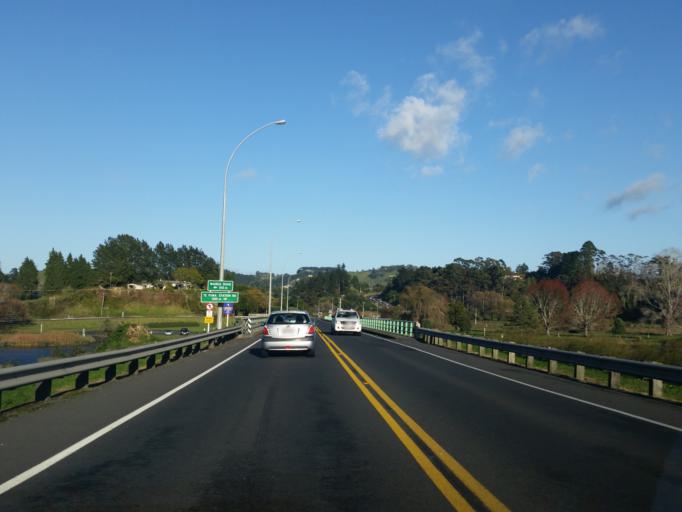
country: NZ
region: Bay of Plenty
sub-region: Tauranga City
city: Tauranga
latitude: -37.6982
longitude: 176.0959
